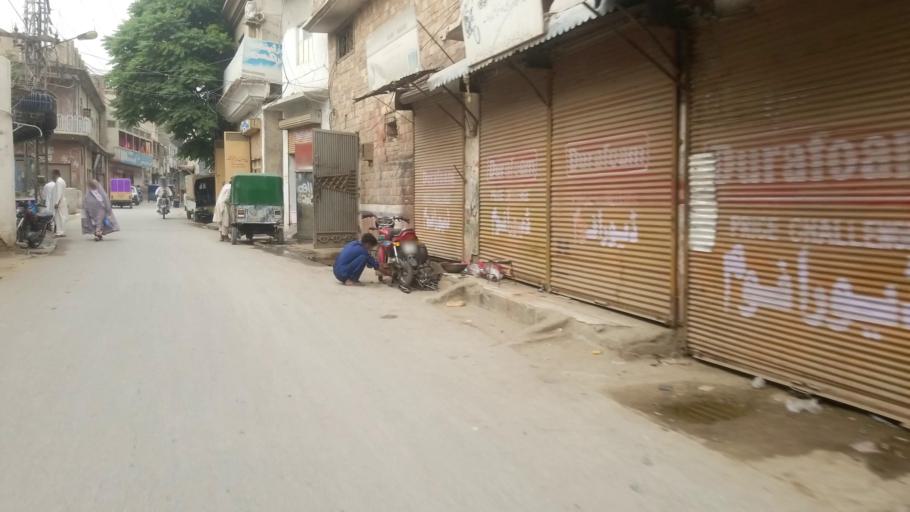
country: PK
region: Khyber Pakhtunkhwa
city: Peshawar
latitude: 33.9997
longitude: 71.5663
